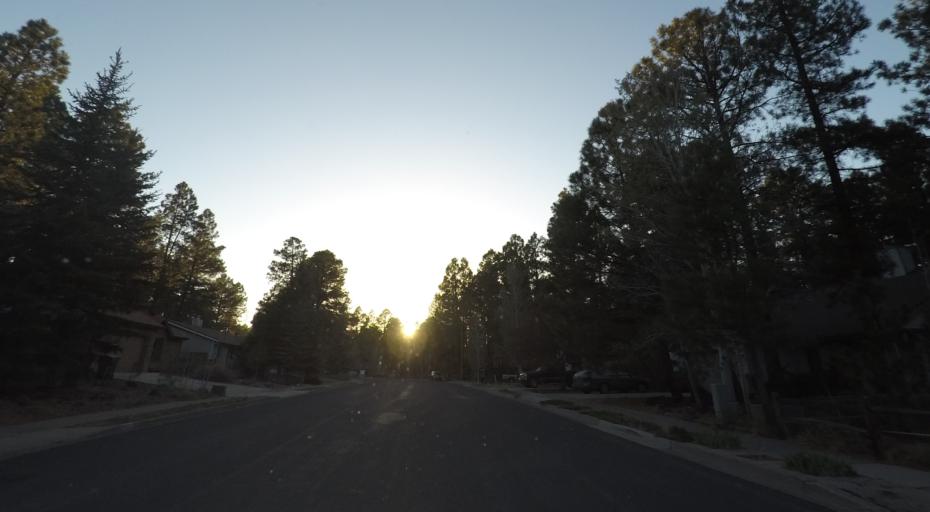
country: US
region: Arizona
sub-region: Coconino County
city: Flagstaff
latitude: 35.1769
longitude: -111.6803
